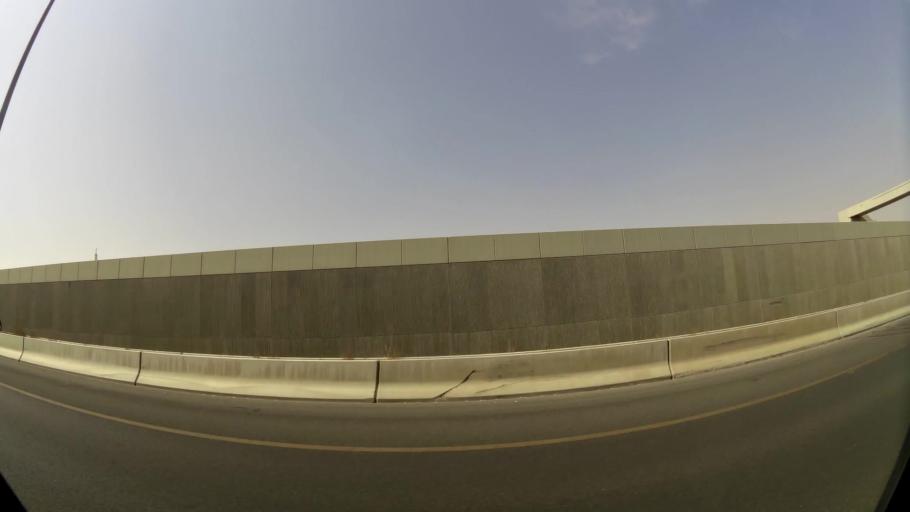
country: KW
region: Al Ahmadi
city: Al Manqaf
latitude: 29.1047
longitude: 48.1181
